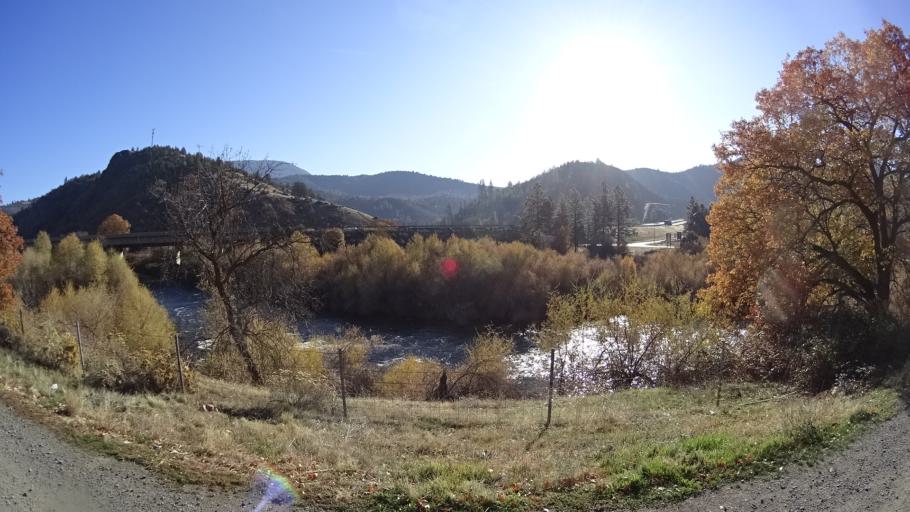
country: US
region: California
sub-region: Siskiyou County
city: Yreka
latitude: 41.8559
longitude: -122.5735
